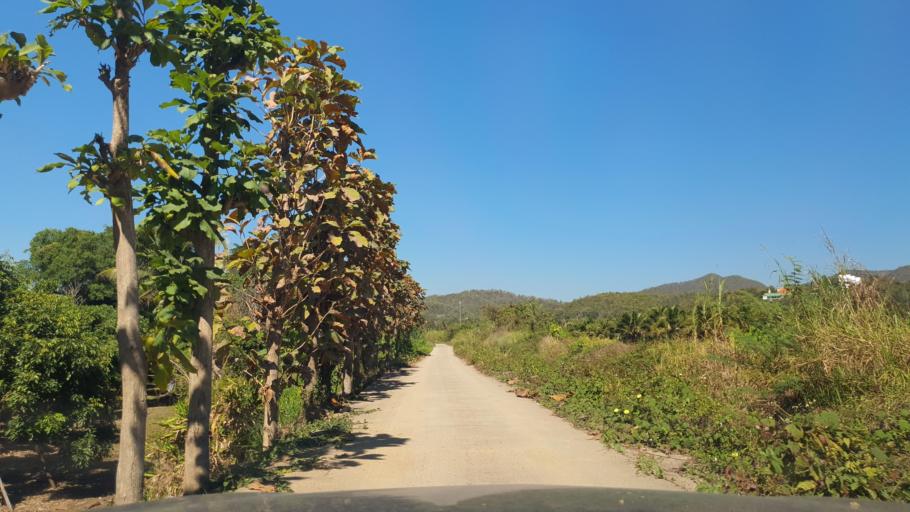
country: TH
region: Chiang Mai
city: San Pa Tong
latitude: 18.6678
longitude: 98.8314
